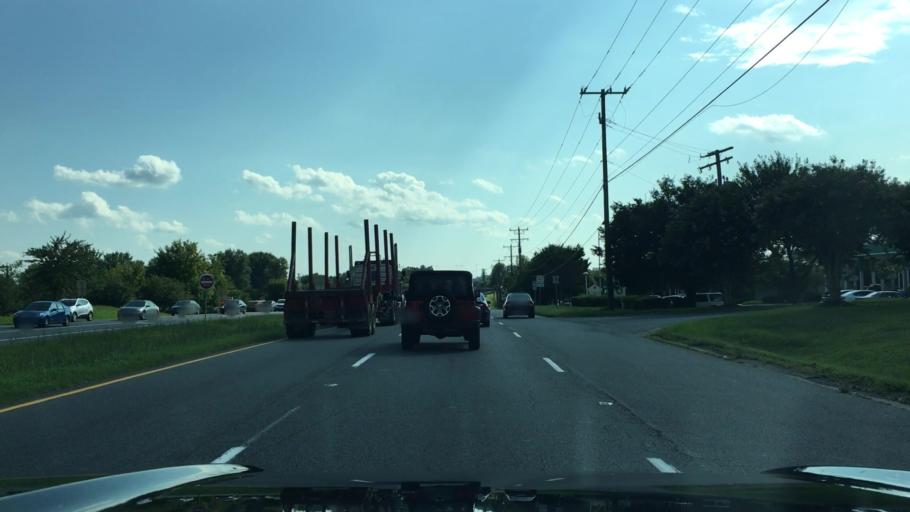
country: US
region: Virginia
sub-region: Albemarle County
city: Hollymead
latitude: 38.1320
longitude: -78.4358
